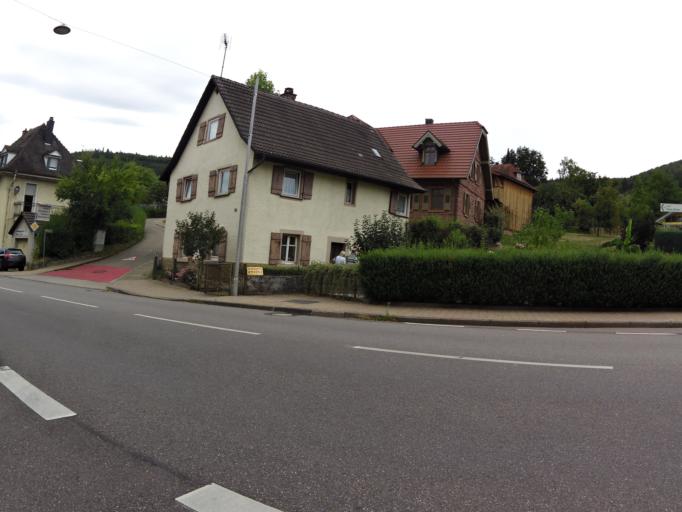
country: DE
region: Baden-Wuerttemberg
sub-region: Freiburg Region
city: Hohberg
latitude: 48.3386
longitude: 7.9088
